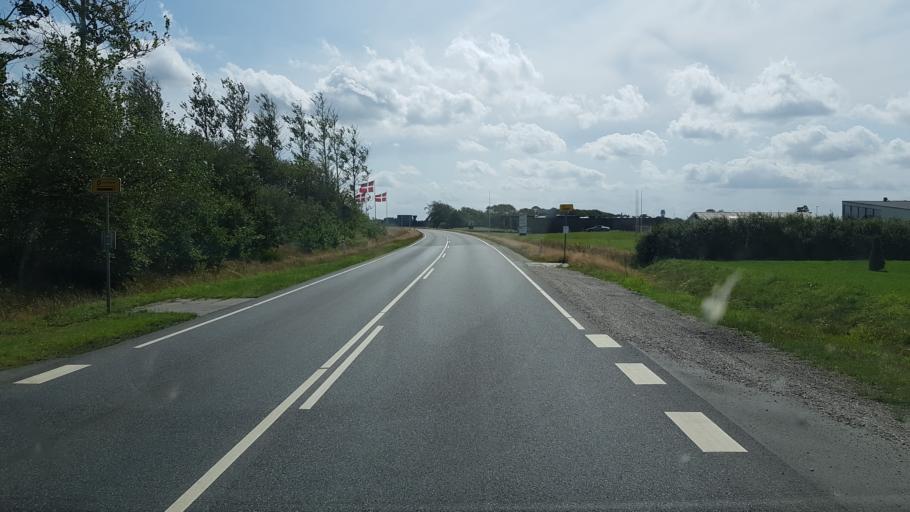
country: DK
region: South Denmark
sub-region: Billund Kommune
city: Billund
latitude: 55.7160
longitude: 9.1290
